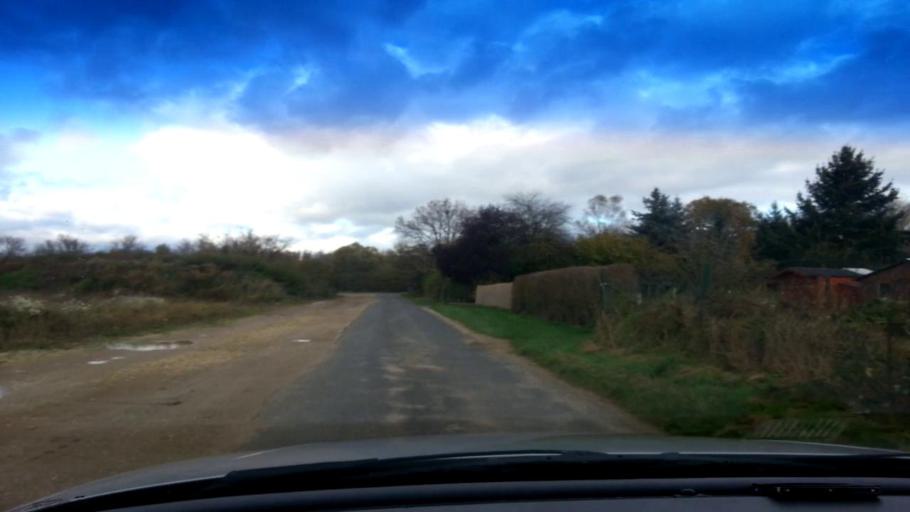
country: DE
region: Bavaria
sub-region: Upper Franconia
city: Zapfendorf
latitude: 50.0236
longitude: 10.9311
